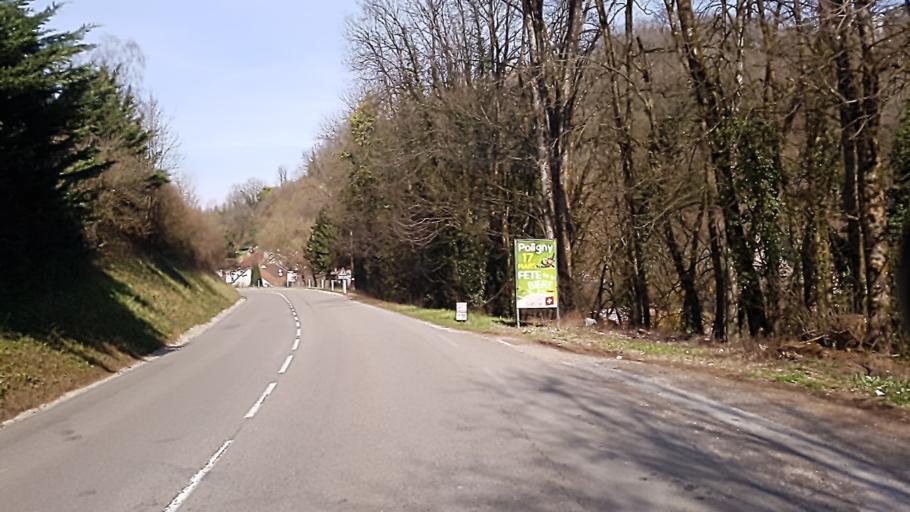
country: FR
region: Franche-Comte
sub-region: Departement du Jura
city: Poligny
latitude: 46.8316
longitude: 5.7149
